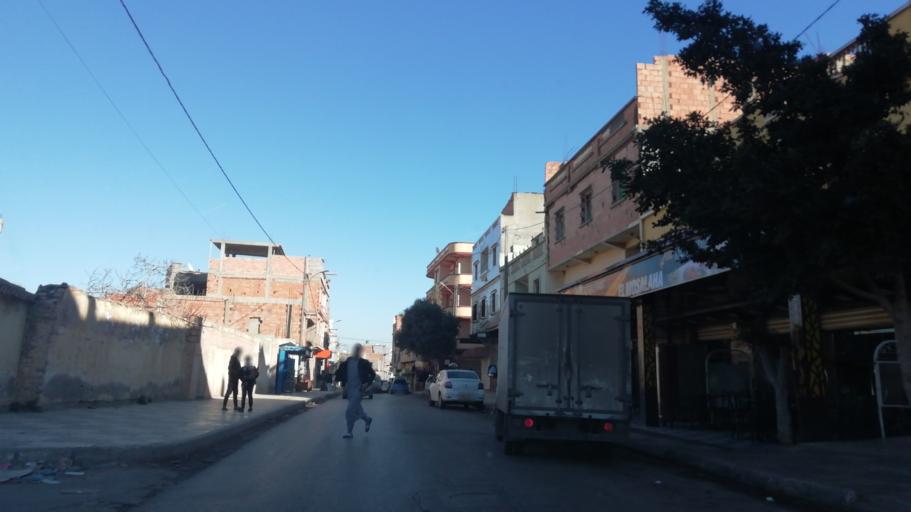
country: DZ
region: Oran
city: Bir el Djir
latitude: 35.7260
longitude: -0.5432
